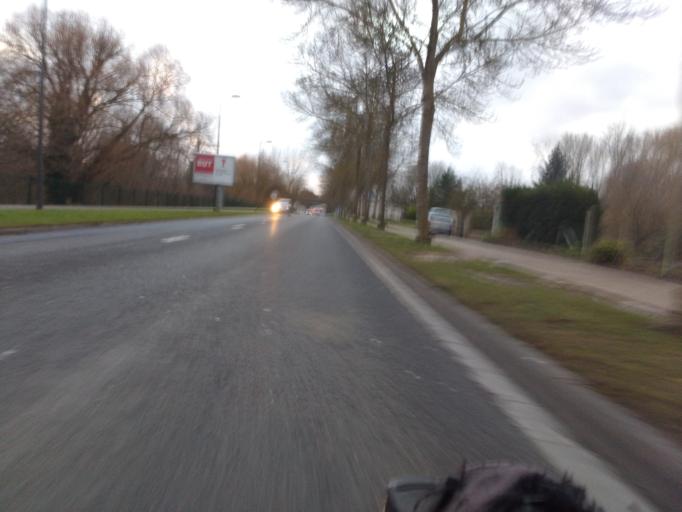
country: FR
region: Picardie
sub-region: Departement de la Somme
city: Camon
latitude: 49.8785
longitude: 2.3378
